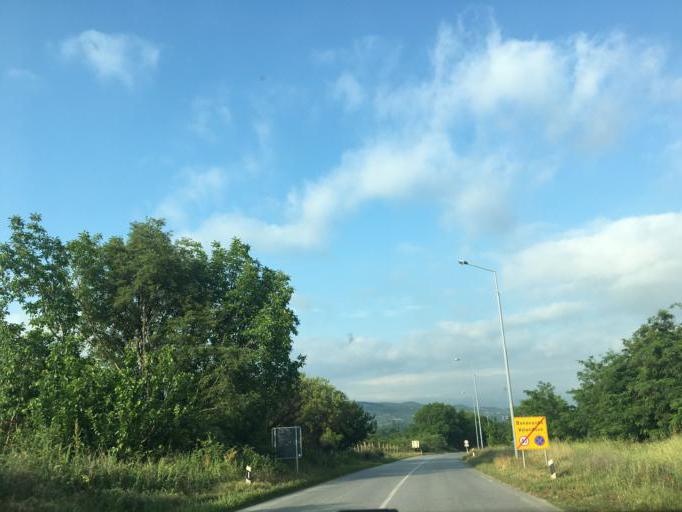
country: MK
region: Valandovo
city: Valandovo
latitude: 41.3146
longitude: 22.5560
